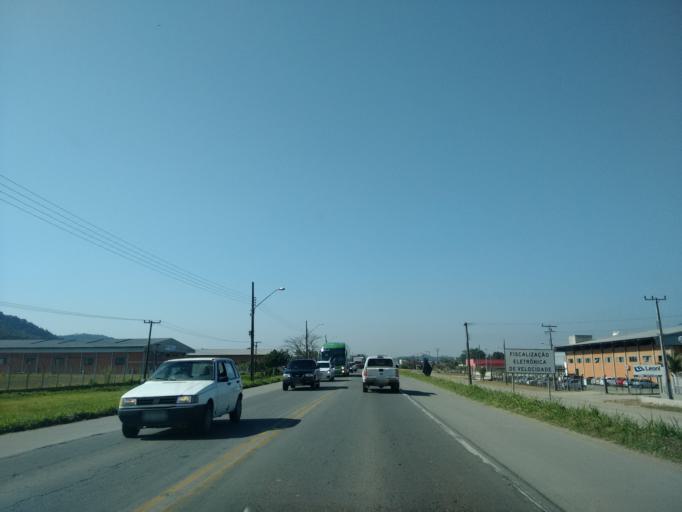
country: BR
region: Santa Catarina
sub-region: Guaramirim
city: Guaramirim
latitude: -26.4730
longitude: -48.9756
